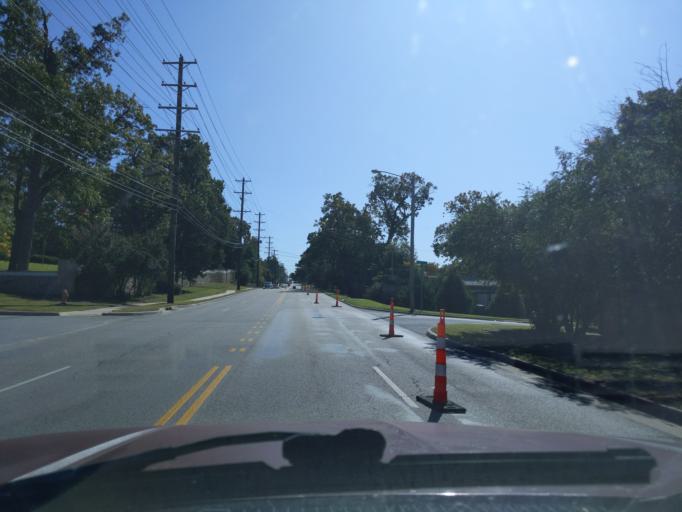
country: US
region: Oklahoma
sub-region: Tulsa County
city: Tulsa
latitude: 36.1144
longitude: -95.9581
